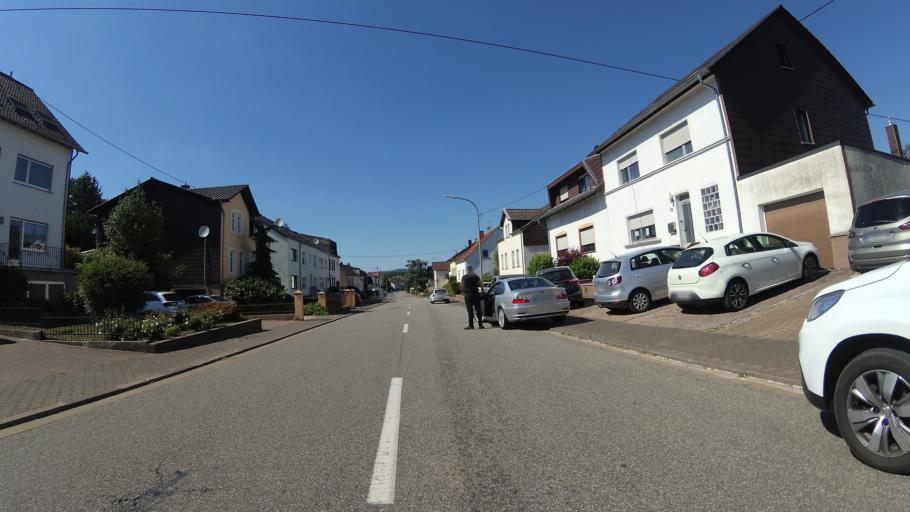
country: DE
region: Saarland
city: Saarwellingen
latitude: 49.3484
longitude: 6.8099
